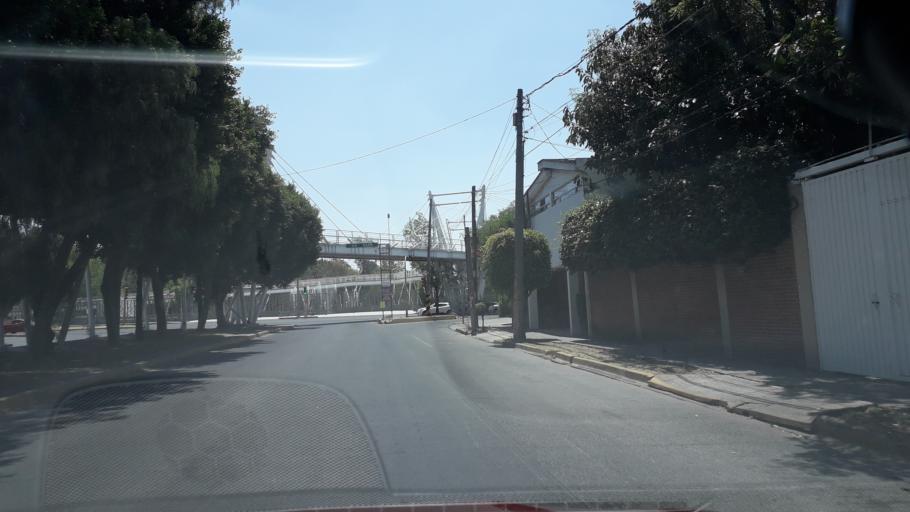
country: MX
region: Puebla
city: Puebla
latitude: 19.0254
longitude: -98.1915
